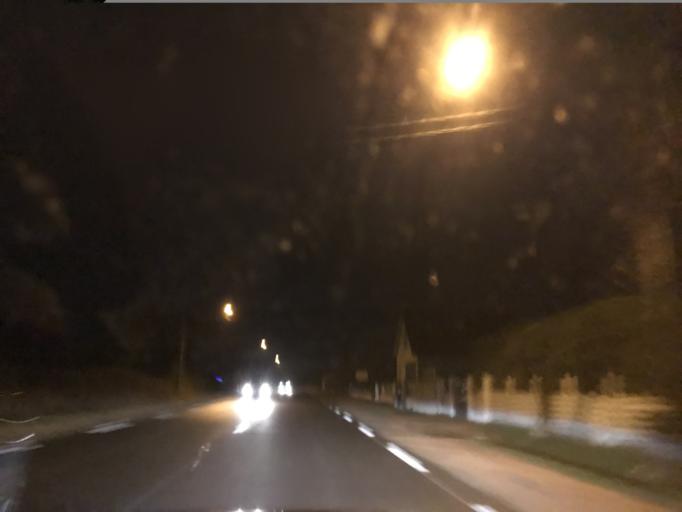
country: FR
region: Auvergne
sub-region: Departement de l'Allier
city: Abrest
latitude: 46.0998
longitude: 3.4294
